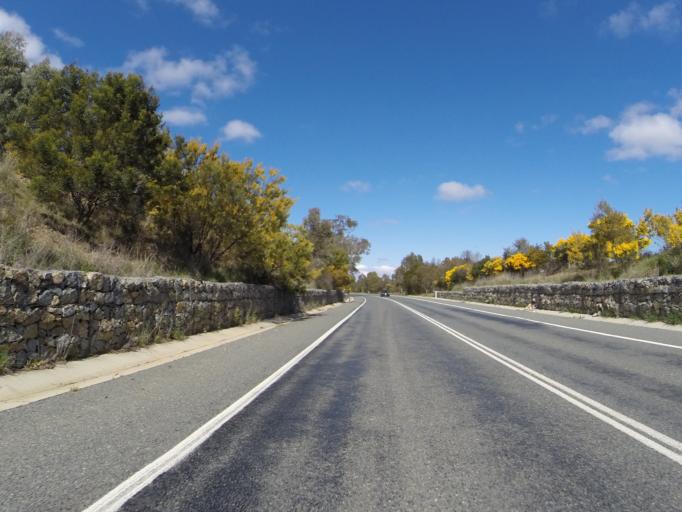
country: AU
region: New South Wales
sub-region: Queanbeyan
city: Queanbeyan
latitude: -35.2923
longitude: 149.2568
